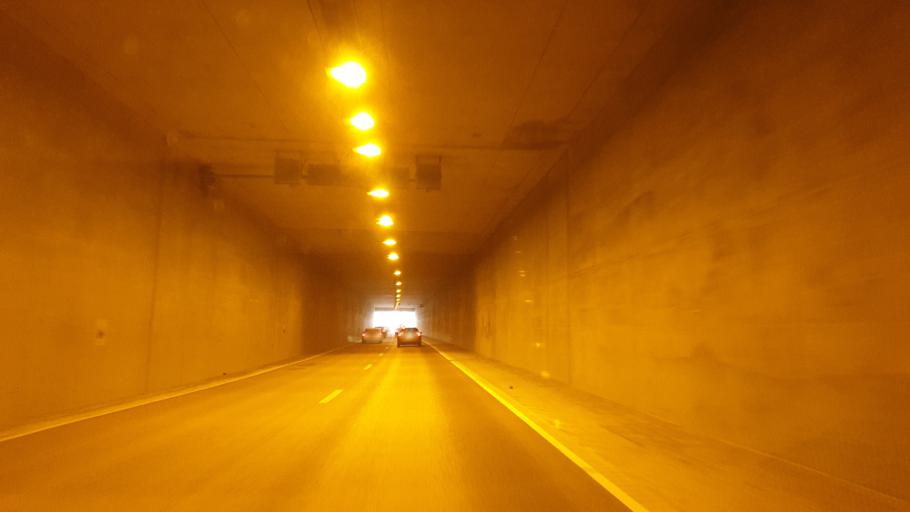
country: SE
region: Stockholm
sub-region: Stockholms Kommun
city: Kista
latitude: 59.3928
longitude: 17.9298
